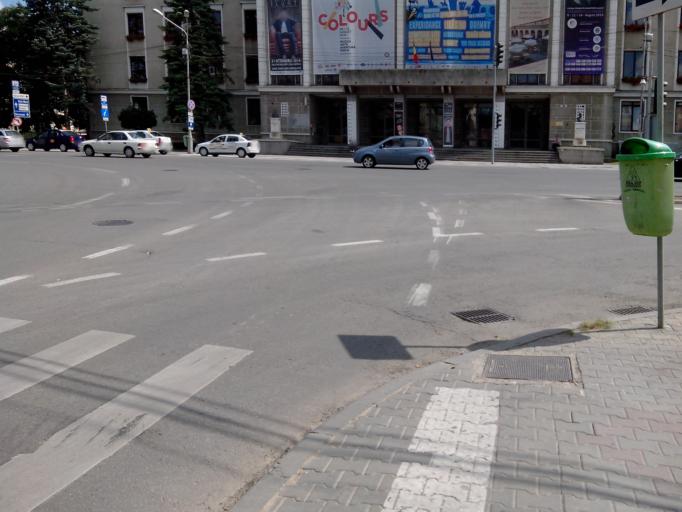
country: RO
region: Cluj
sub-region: Municipiul Cluj-Napoca
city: Cluj-Napoca
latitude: 46.7676
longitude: 23.5860
